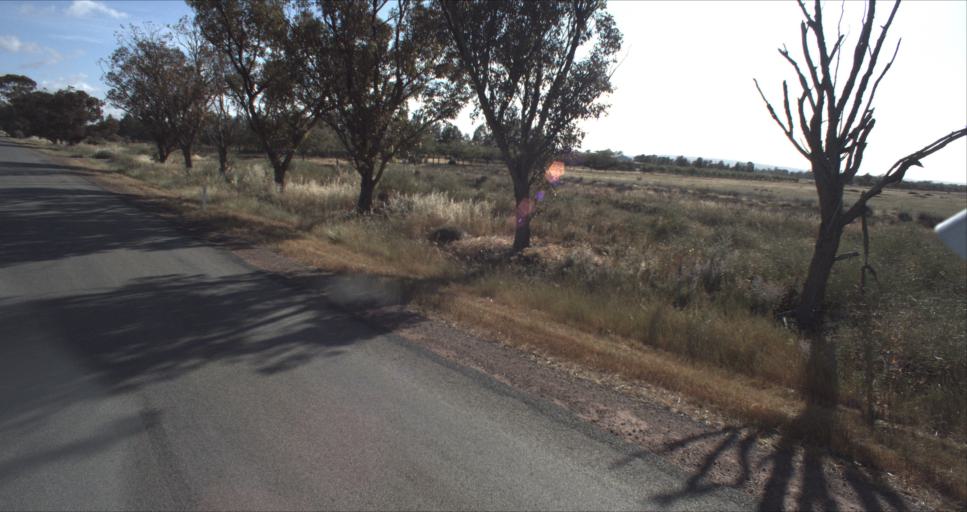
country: AU
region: New South Wales
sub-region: Leeton
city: Leeton
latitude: -34.5220
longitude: 146.3904
